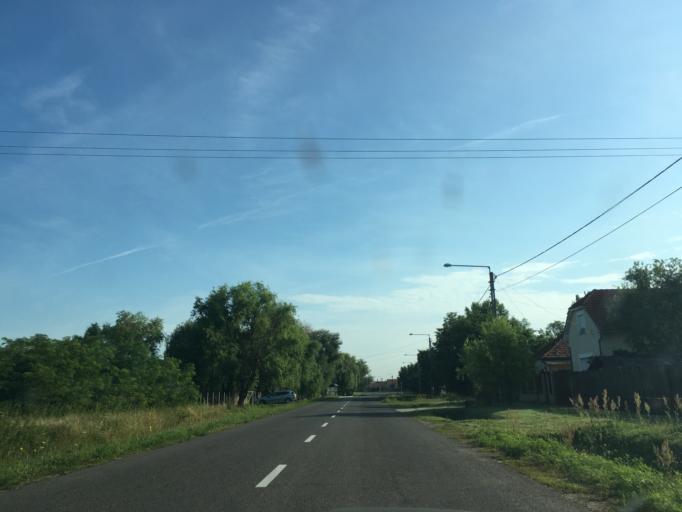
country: HU
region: Hajdu-Bihar
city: Hajdusamson
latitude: 47.5920
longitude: 21.7620
